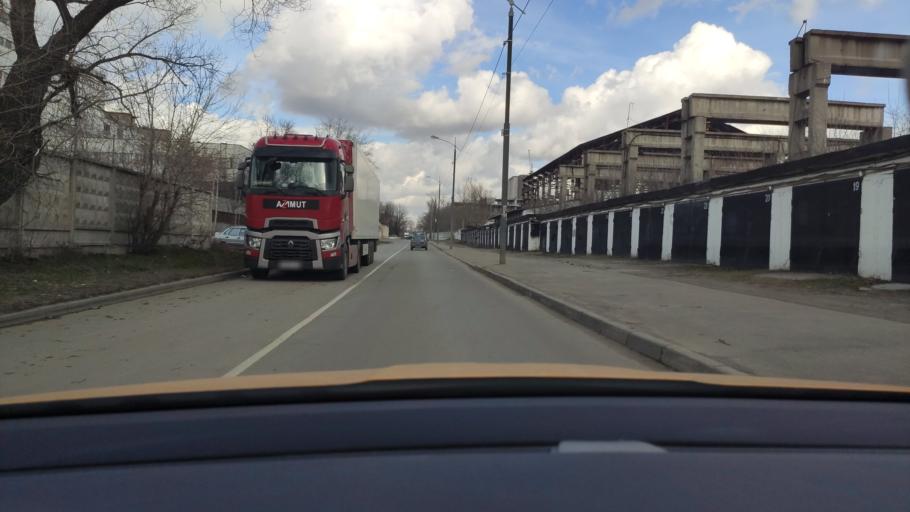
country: RU
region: Moscow
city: Ryazanskiy
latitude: 55.7181
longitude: 37.7642
